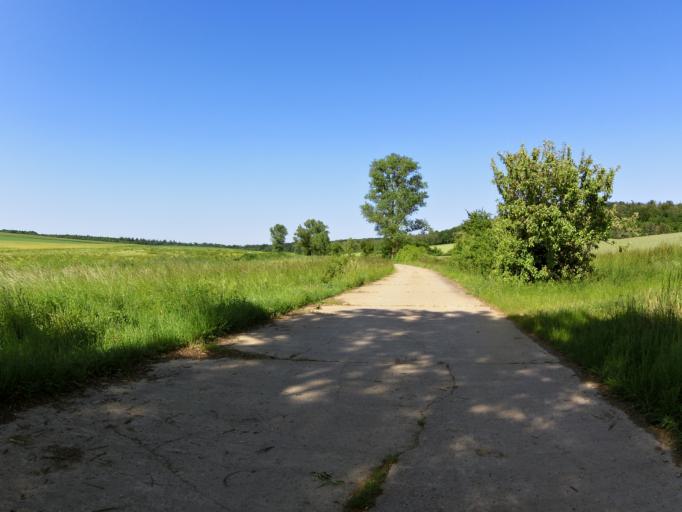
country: DE
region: Bavaria
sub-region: Regierungsbezirk Unterfranken
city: Kleinrinderfeld
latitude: 49.7054
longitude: 9.8525
